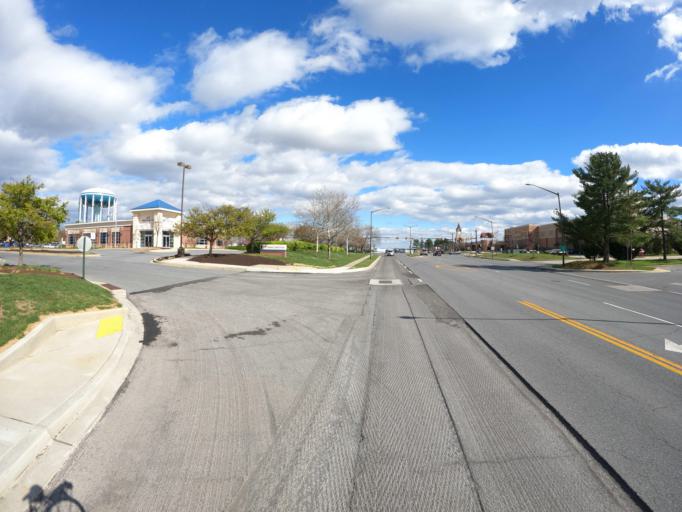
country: US
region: Maryland
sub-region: Howard County
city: Savage
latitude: 39.1877
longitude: -76.8201
